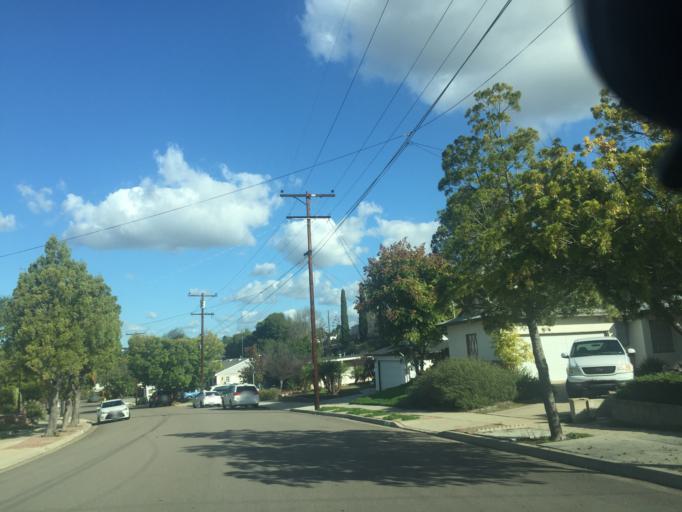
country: US
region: California
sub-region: San Diego County
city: La Mesa
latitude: 32.7909
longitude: -117.0891
